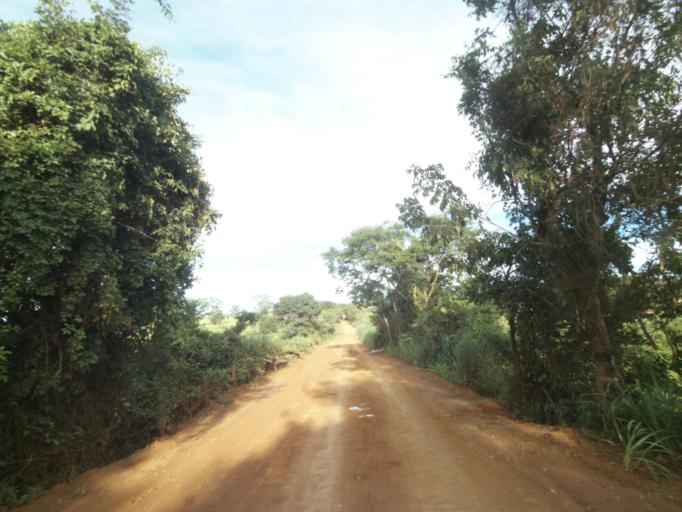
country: BR
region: Goias
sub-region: Jaragua
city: Jaragua
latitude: -15.8886
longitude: -49.4654
